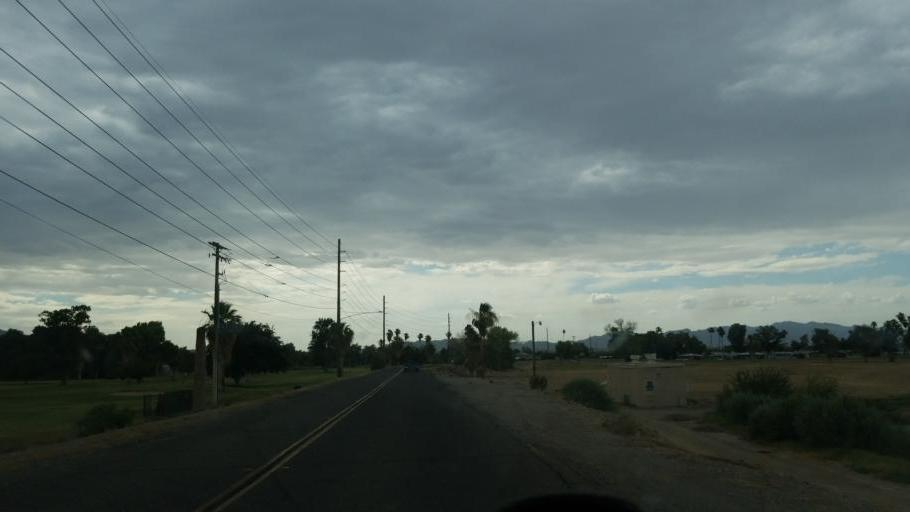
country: US
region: California
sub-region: San Bernardino County
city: Needles
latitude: 34.8442
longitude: -114.6033
